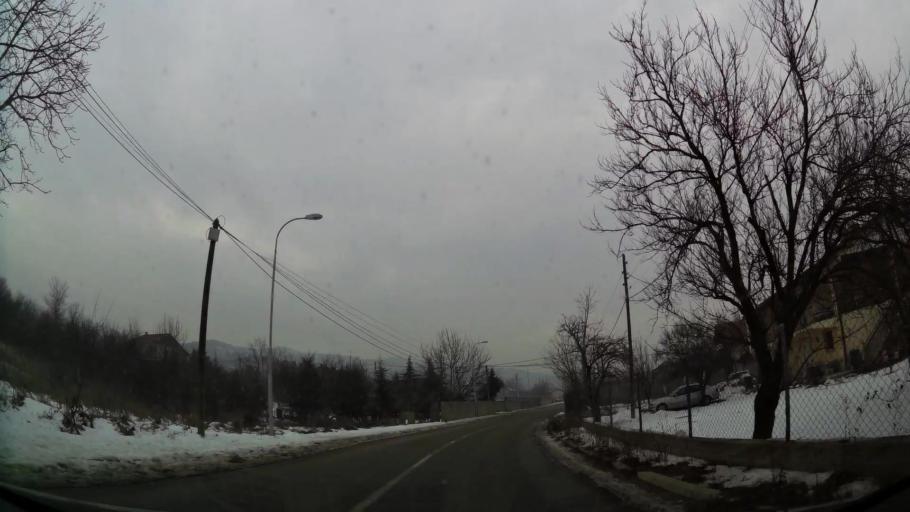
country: MK
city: Kondovo
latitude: 42.0495
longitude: 21.3466
